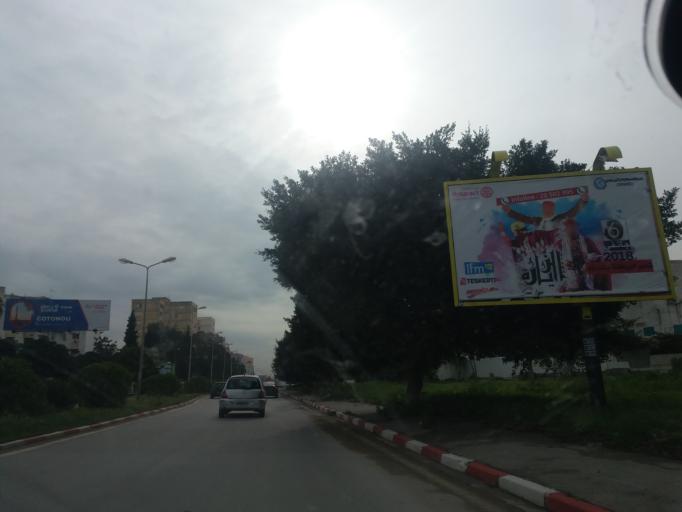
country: TN
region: Tunis
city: Tunis
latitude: 36.8478
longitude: 10.1587
